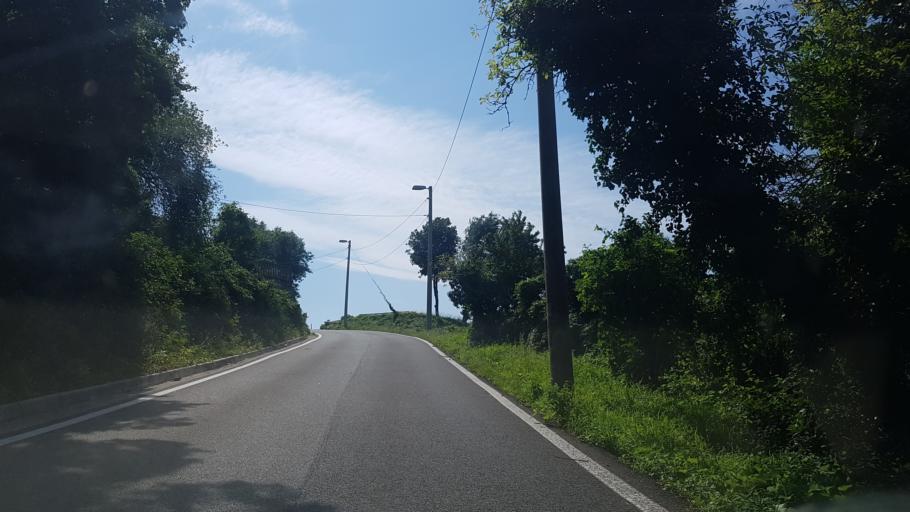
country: IT
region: Friuli Venezia Giulia
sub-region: Provincia di Trieste
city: Villa Opicina
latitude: 45.6705
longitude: 13.7929
